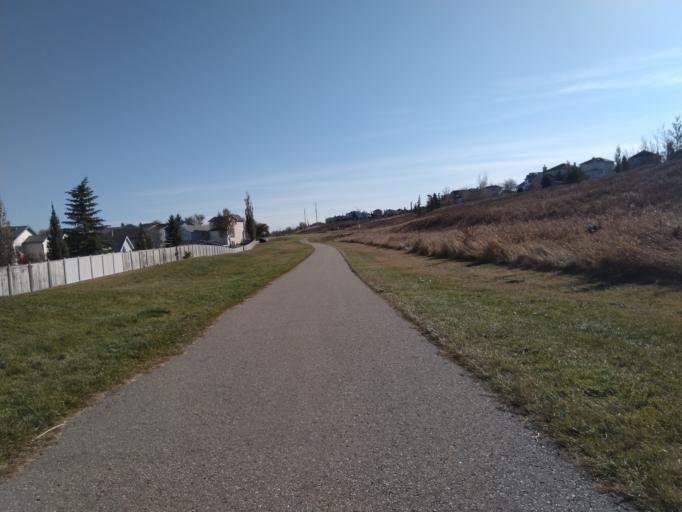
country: CA
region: Alberta
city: Calgary
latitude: 51.1527
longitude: -114.1150
